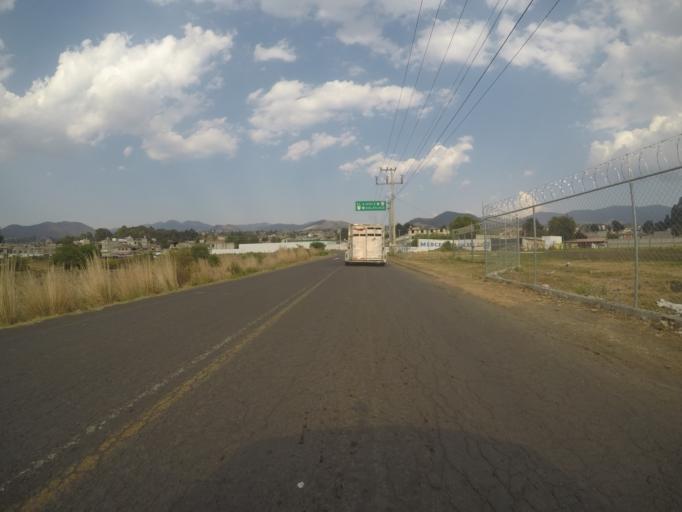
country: MX
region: Mexico
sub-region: Xalatlaco
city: Techichili
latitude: 19.1719
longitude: -99.4137
